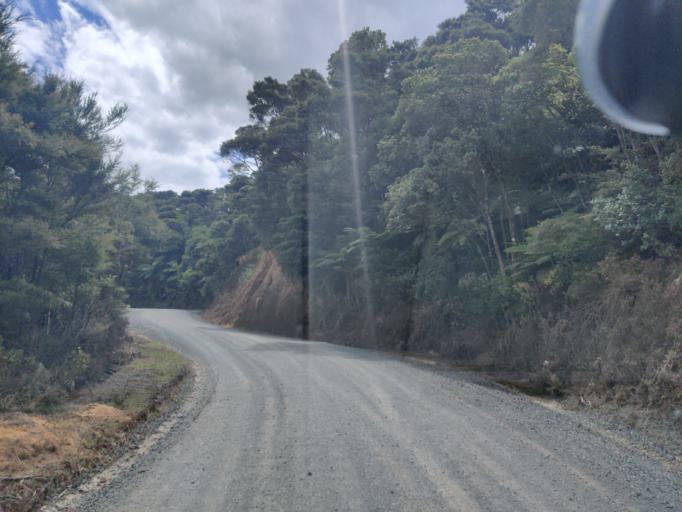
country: NZ
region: Northland
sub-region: Far North District
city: Paihia
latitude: -35.2613
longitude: 174.0485
